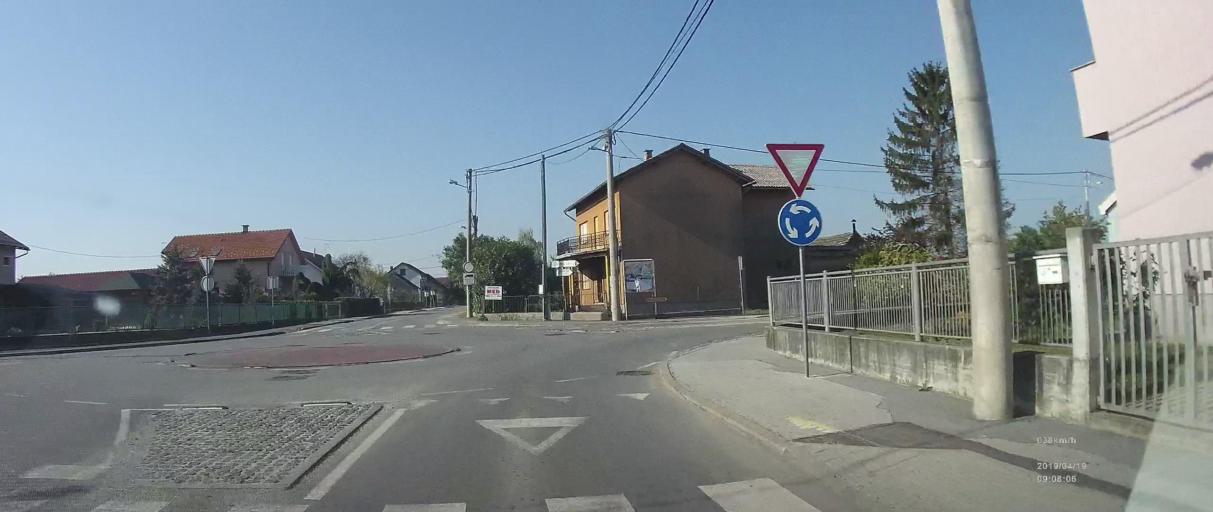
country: HR
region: Zagrebacka
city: Gradici
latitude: 45.7122
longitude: 16.0439
